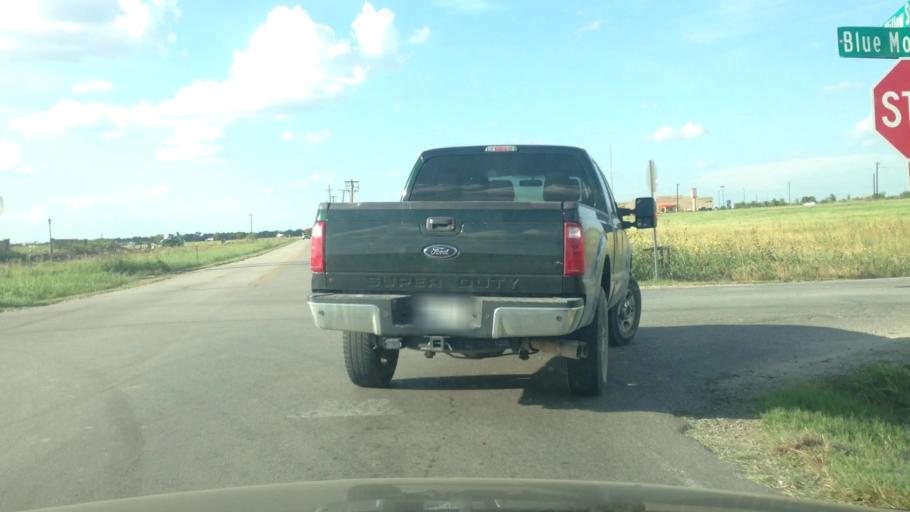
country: US
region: Texas
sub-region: Tarrant County
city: Haslet
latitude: 32.9463
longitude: -97.3920
